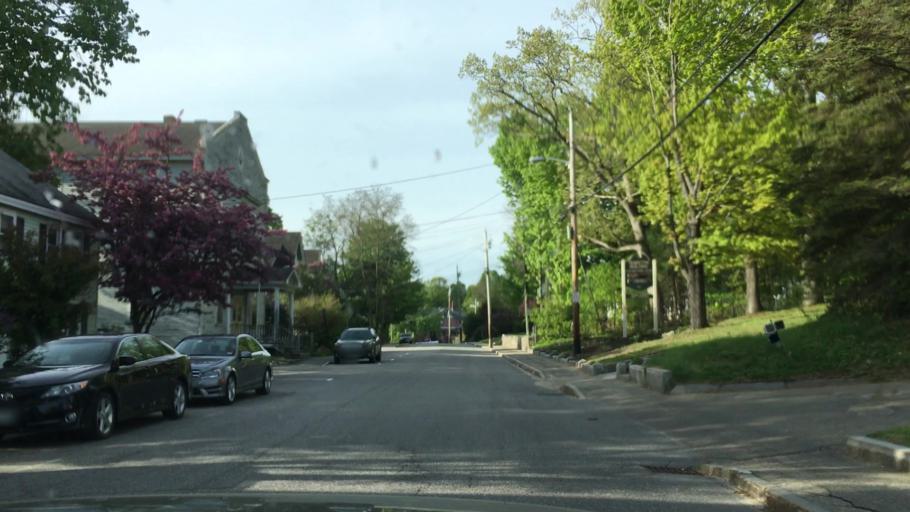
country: US
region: New Hampshire
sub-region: Belknap County
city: Meredith
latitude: 43.6551
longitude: -71.5002
